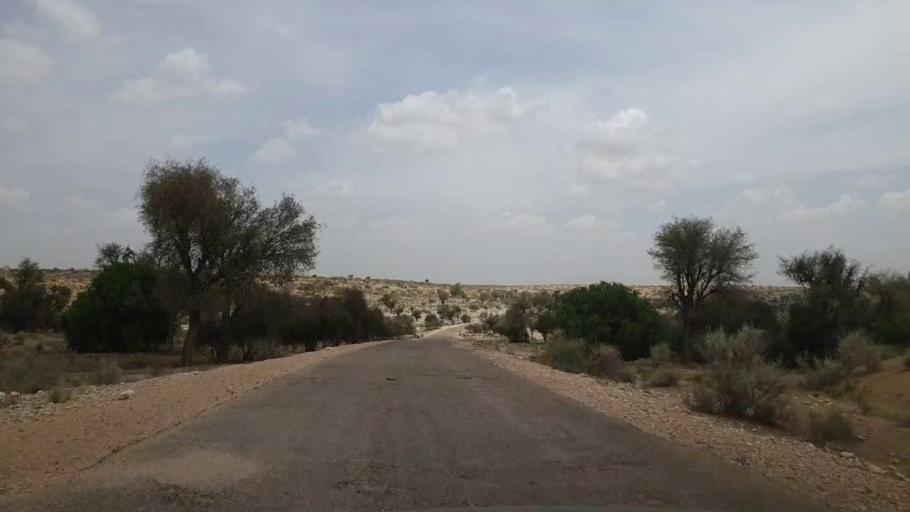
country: PK
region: Sindh
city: Kot Diji
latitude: 27.1810
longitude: 69.1837
